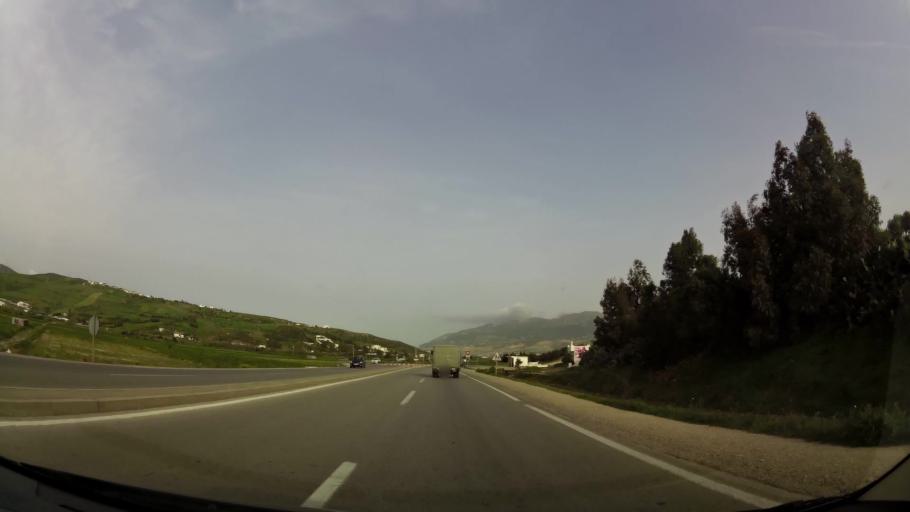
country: MA
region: Tanger-Tetouan
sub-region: Tetouan
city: Saddina
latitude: 35.5604
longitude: -5.4685
